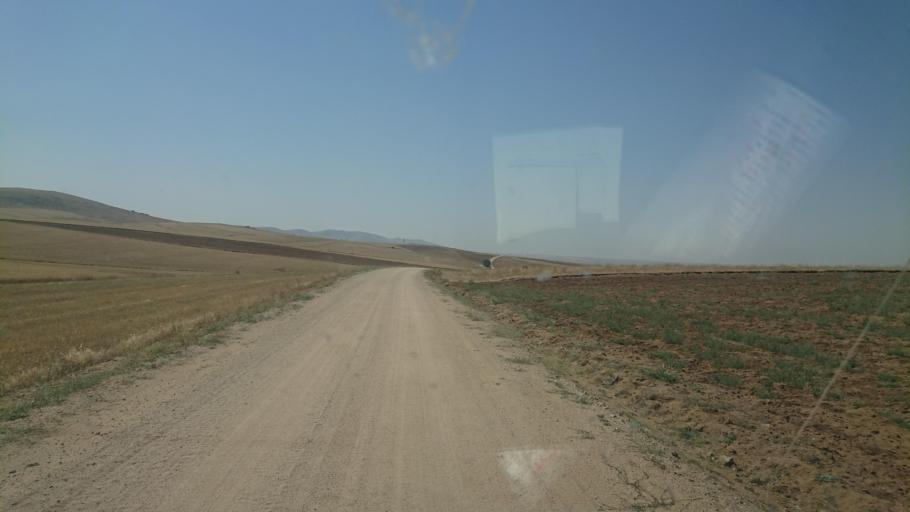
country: TR
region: Aksaray
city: Agacoren
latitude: 38.7967
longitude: 33.9421
